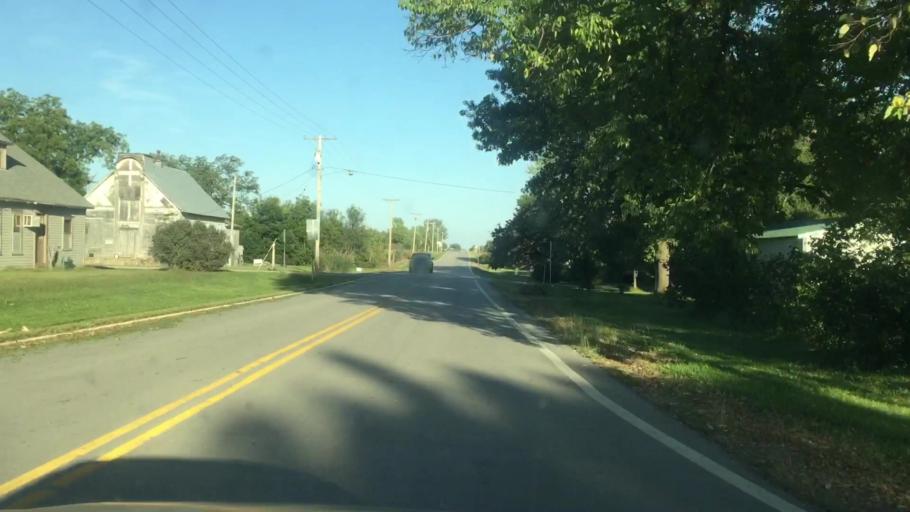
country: US
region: Kansas
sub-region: Brown County
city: Horton
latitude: 39.5876
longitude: -95.6116
